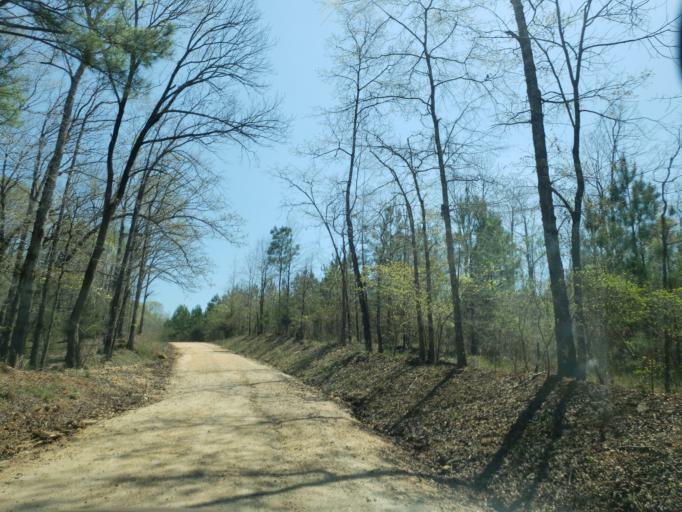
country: US
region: Alabama
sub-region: Tallapoosa County
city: Camp Hill
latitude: 32.6555
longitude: -85.6615
